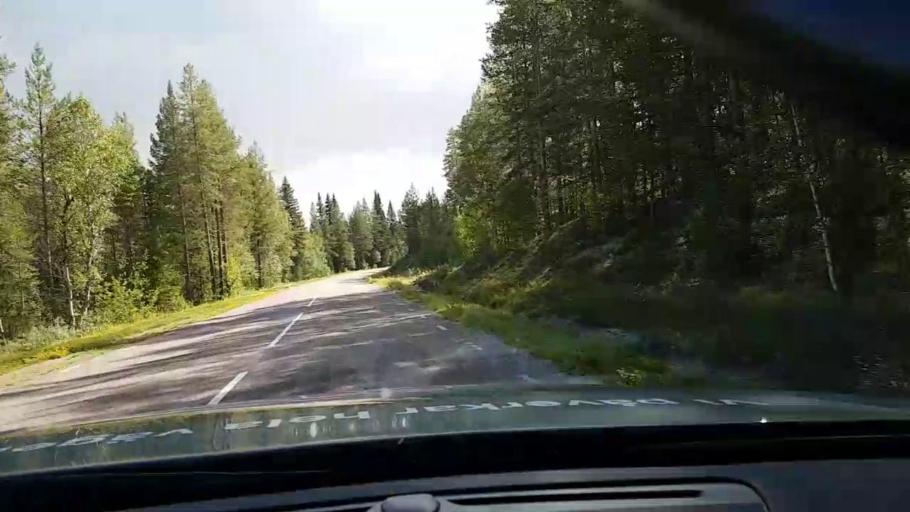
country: SE
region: Vaesterbotten
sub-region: Asele Kommun
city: Asele
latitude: 63.8775
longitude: 17.3565
